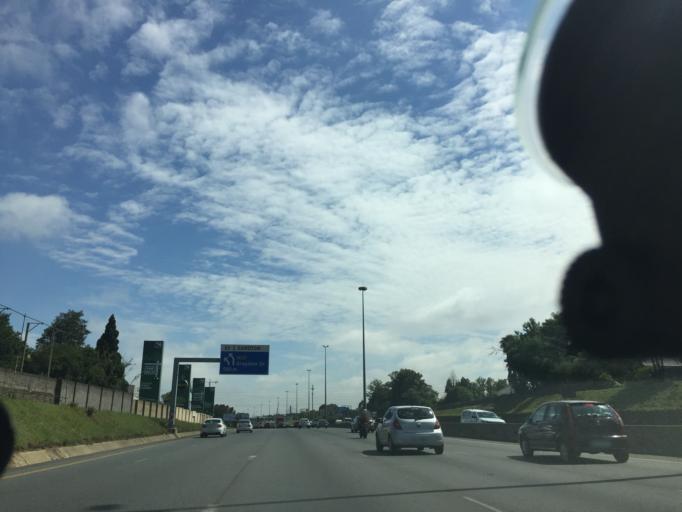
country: ZA
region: Gauteng
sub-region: City of Johannesburg Metropolitan Municipality
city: Johannesburg
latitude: -26.1170
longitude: 28.0742
